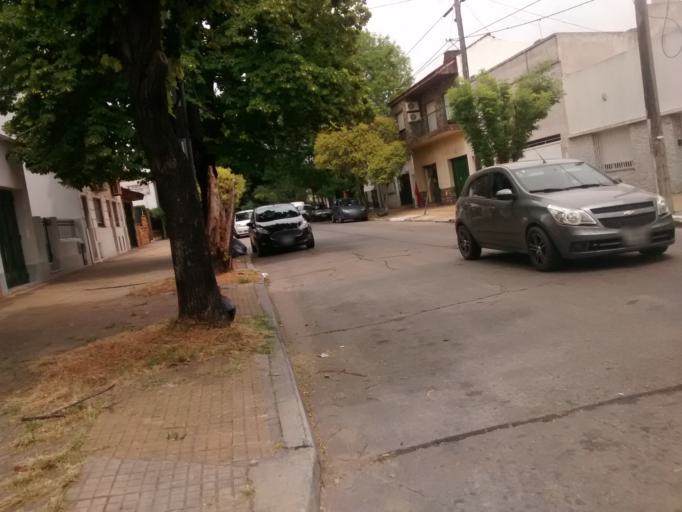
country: AR
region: Buenos Aires
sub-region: Partido de La Plata
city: La Plata
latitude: -34.9165
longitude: -57.9658
